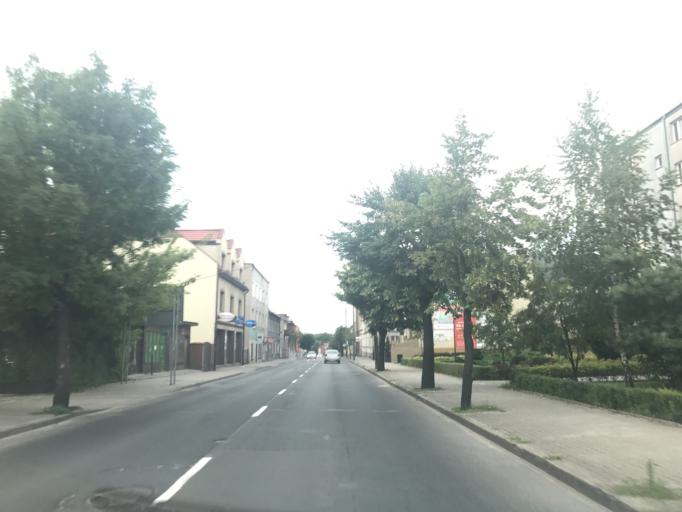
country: PL
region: Kujawsko-Pomorskie
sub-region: Powiat lipnowski
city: Lipno
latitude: 52.8425
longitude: 19.1774
